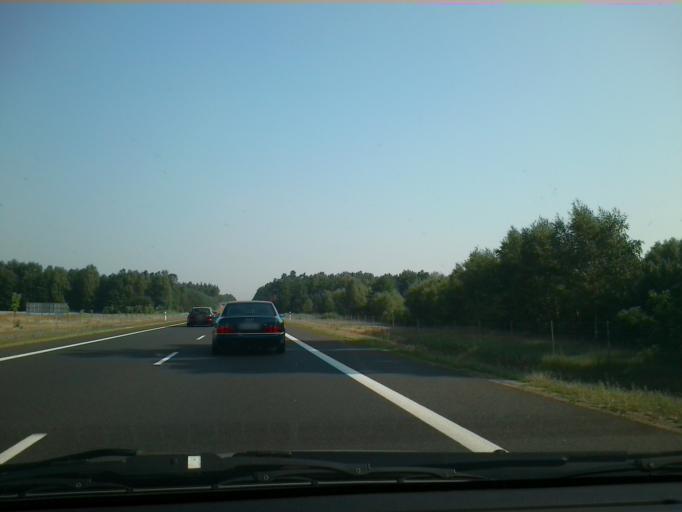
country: PL
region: Lubusz
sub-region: Powiat nowosolski
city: Nowa Sol
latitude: 51.8063
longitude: 15.6765
